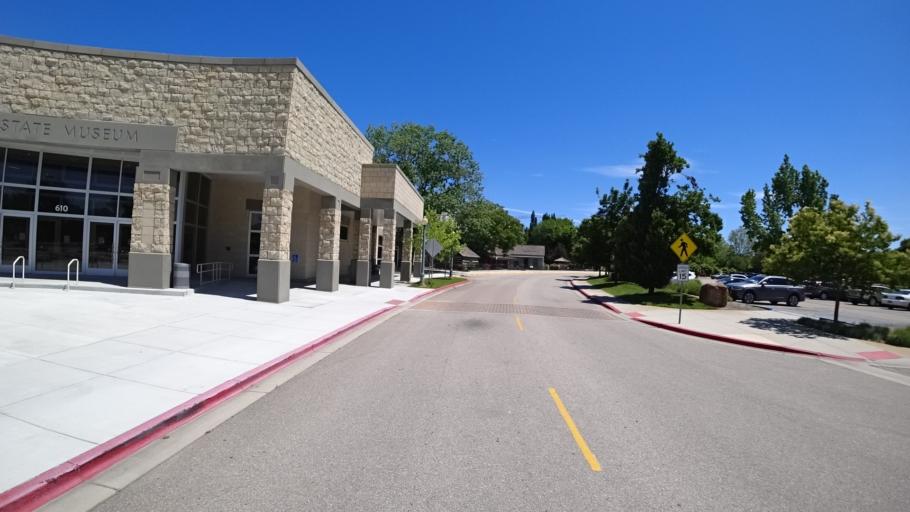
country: US
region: Idaho
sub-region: Ada County
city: Boise
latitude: 43.6103
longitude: -116.2058
